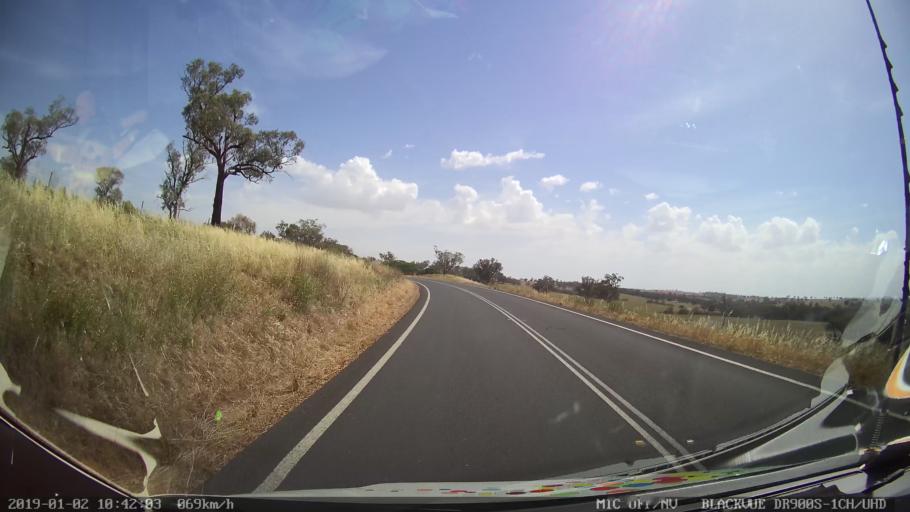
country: AU
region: New South Wales
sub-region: Cootamundra
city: Cootamundra
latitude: -34.7889
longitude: 148.3086
